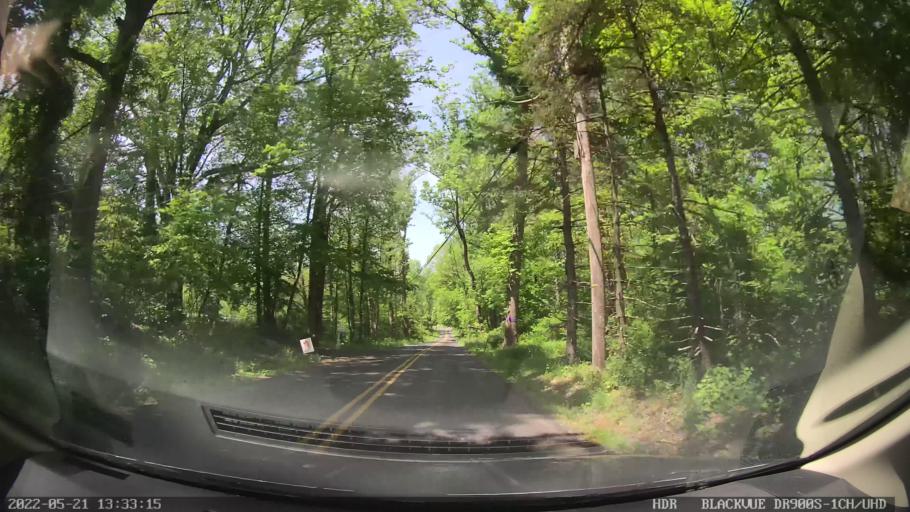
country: US
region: Pennsylvania
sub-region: Berks County
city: Red Lion
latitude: 40.4371
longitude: -75.6676
